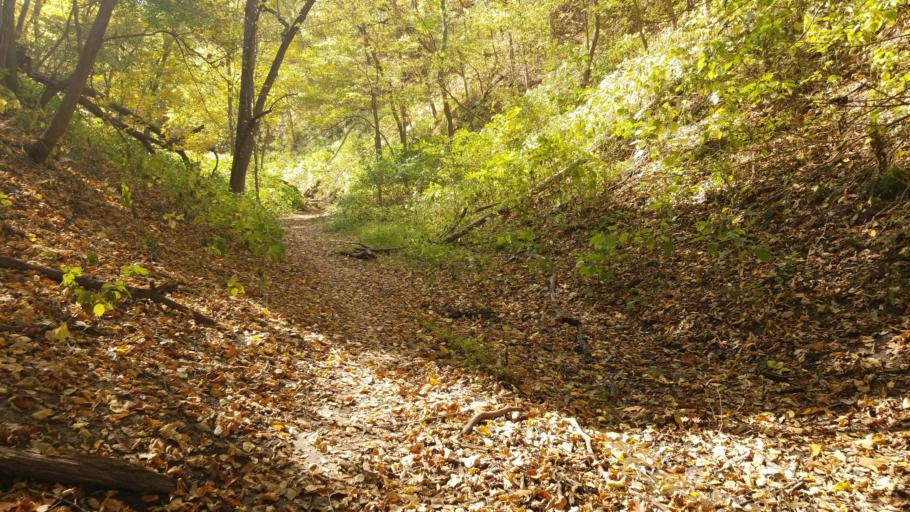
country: US
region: Nebraska
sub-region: Sarpy County
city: Bellevue
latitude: 41.1797
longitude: -95.9008
